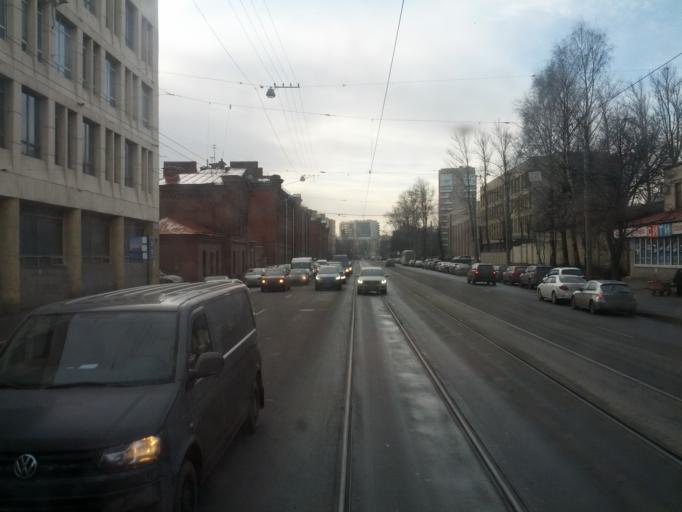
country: RU
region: St.-Petersburg
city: Centralniy
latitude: 59.9406
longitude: 30.4086
